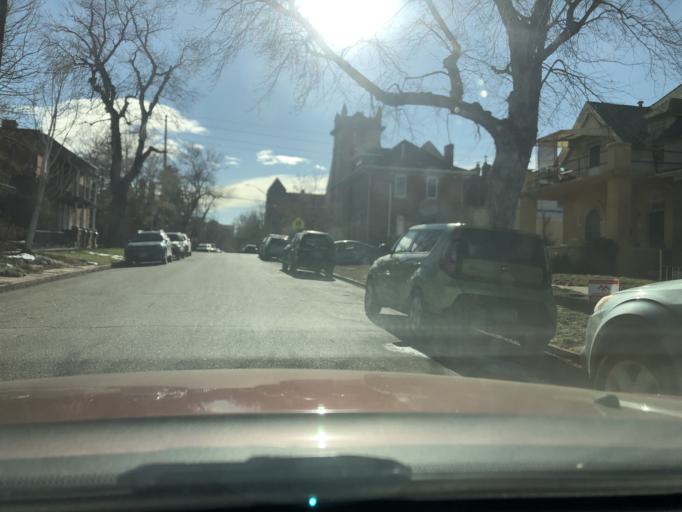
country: US
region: Colorado
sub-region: Denver County
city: Denver
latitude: 39.7514
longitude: -104.9746
